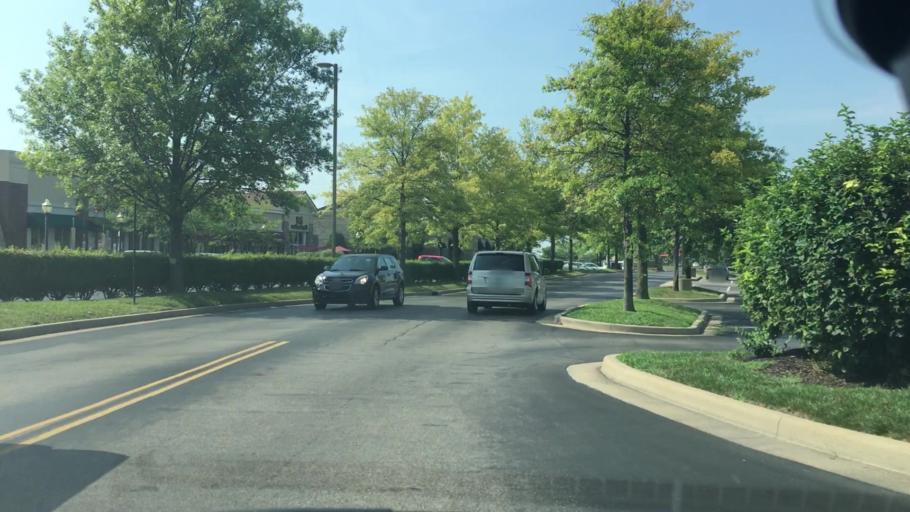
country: US
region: Indiana
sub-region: Vanderburgh County
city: Melody Hill
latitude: 37.9746
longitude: -87.4721
